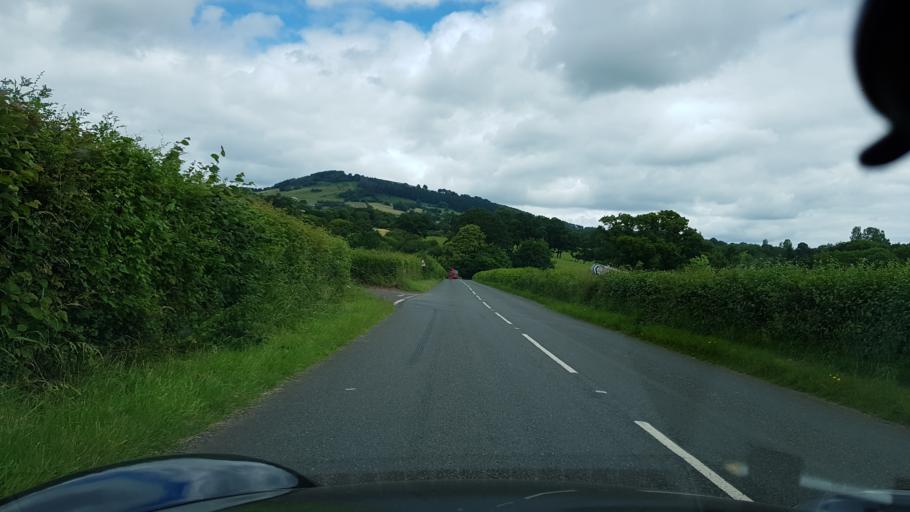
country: GB
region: Wales
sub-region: Monmouthshire
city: Grosmont
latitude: 51.8639
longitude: -2.8845
